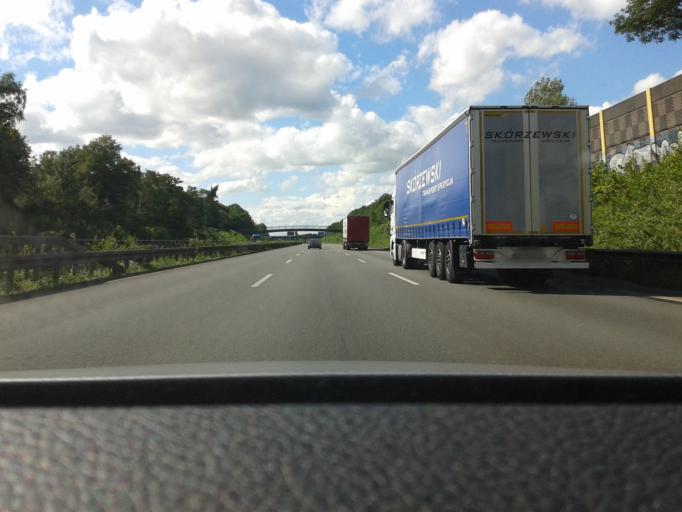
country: DE
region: North Rhine-Westphalia
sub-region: Regierungsbezirk Dusseldorf
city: Moers
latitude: 51.4368
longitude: 6.6549
